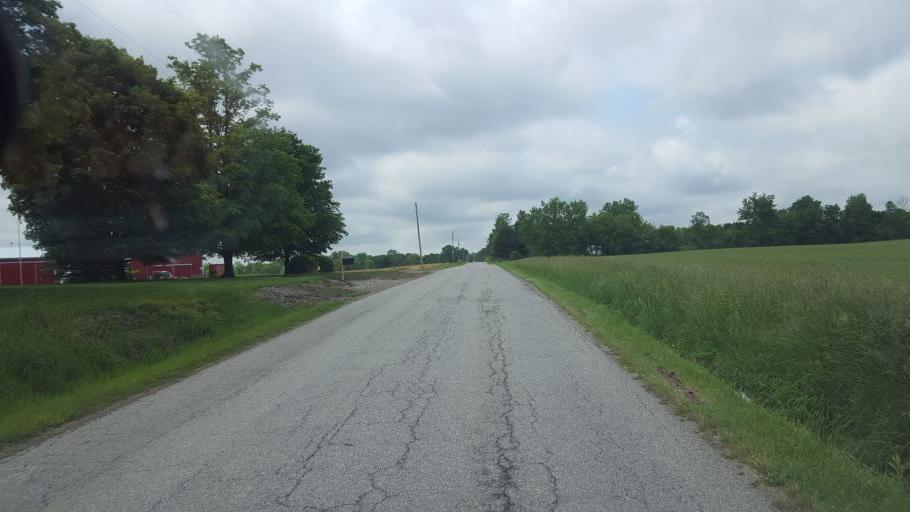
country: US
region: Ohio
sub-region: Delaware County
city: Ashley
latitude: 40.3829
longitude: -82.8846
